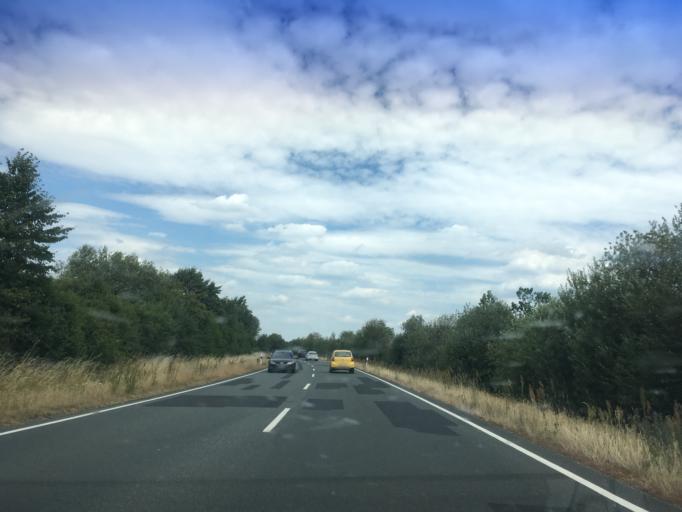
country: DE
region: Saxony
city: Goerlitz
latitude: 51.1573
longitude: 14.9533
